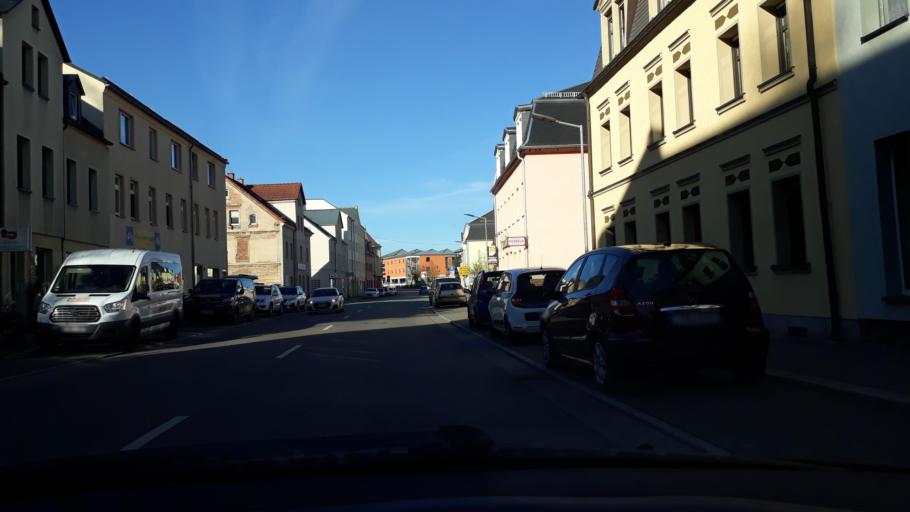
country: DE
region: Saxony
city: Wilkau-Hasslau
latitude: 50.6727
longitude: 12.5174
